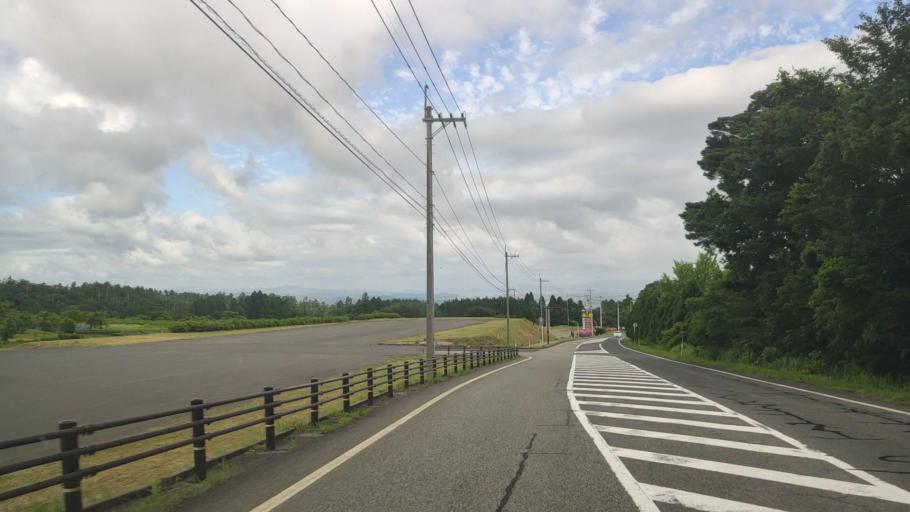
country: JP
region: Tottori
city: Yonago
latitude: 35.4095
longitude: 133.4772
